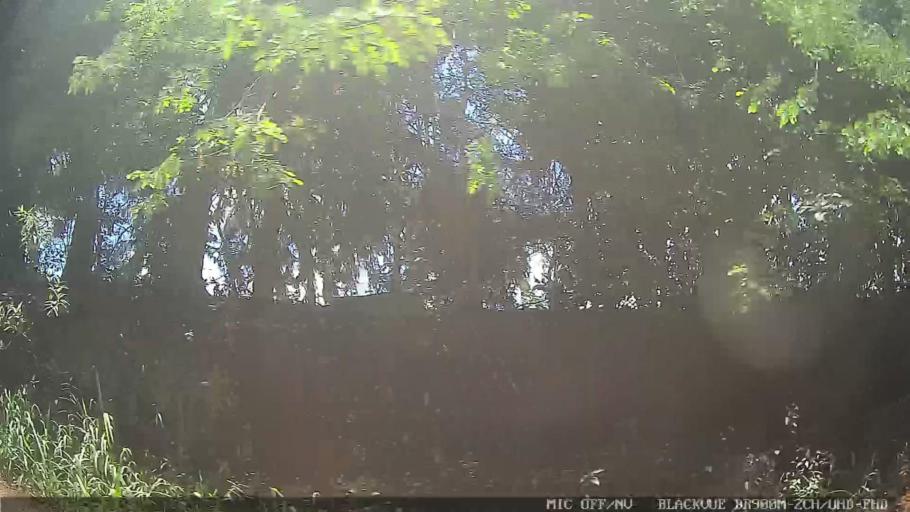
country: BR
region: Sao Paulo
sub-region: Braganca Paulista
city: Braganca Paulista
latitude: -23.0271
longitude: -46.4724
